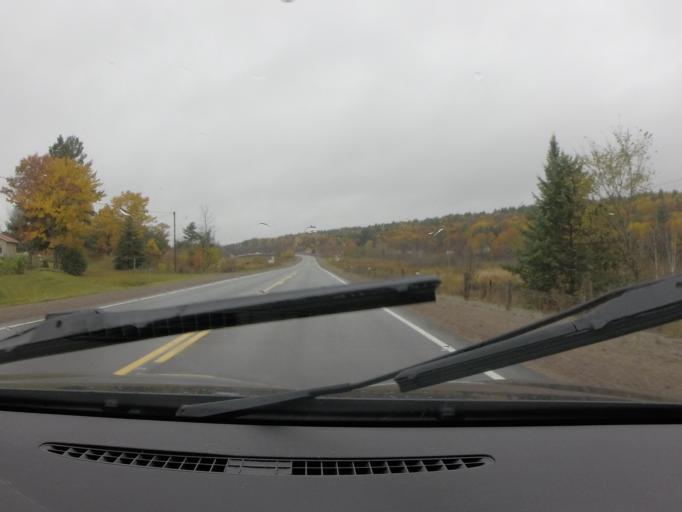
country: CA
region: Ontario
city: Greater Napanee
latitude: 44.6587
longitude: -77.0971
